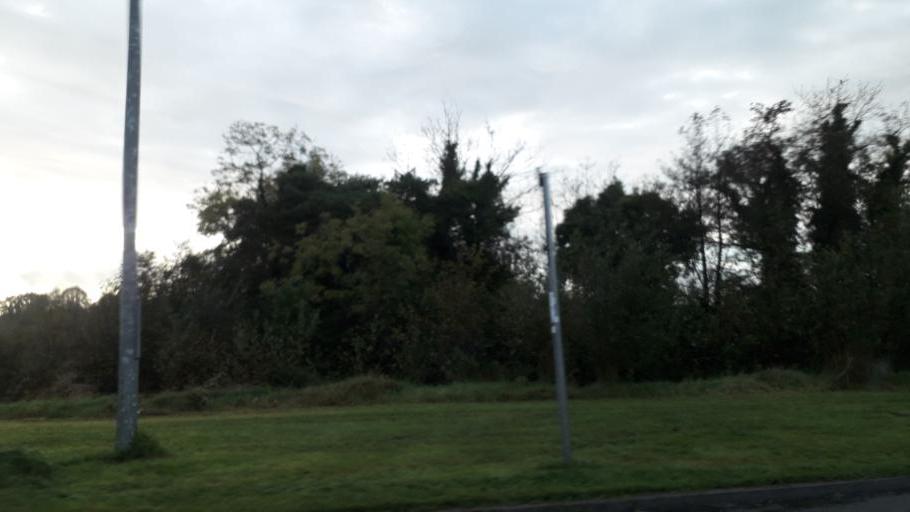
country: IE
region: Leinster
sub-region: An Longfort
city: Longford
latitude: 53.7443
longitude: -7.8084
